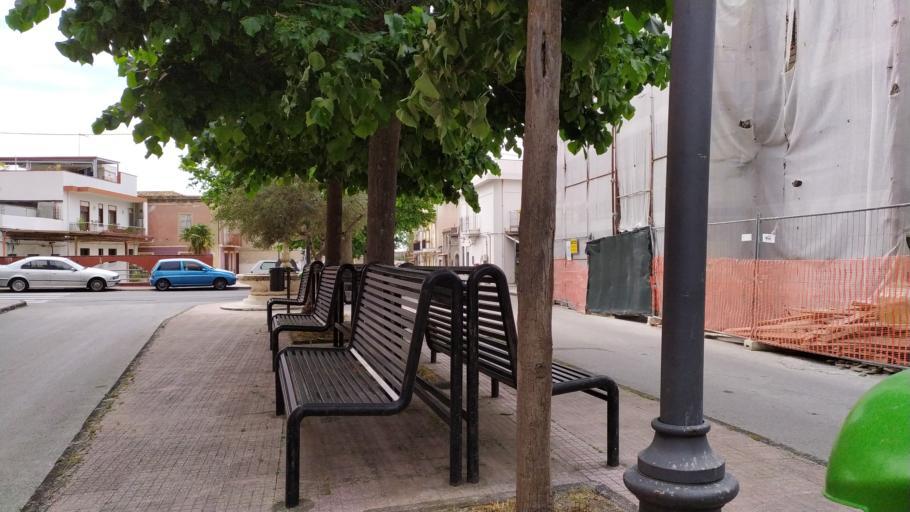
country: IT
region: Sicily
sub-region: Messina
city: San Filippo del Mela
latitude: 38.1817
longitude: 15.2710
